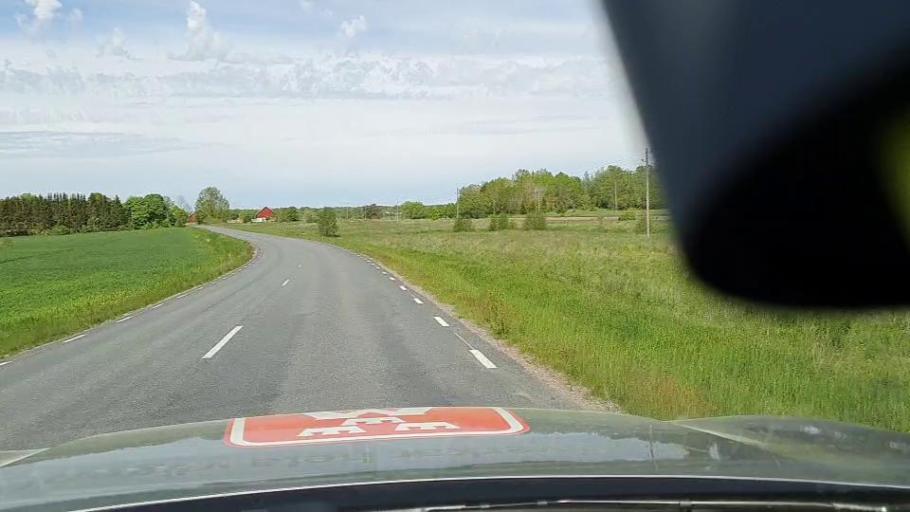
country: SE
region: Soedermanland
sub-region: Eskilstuna Kommun
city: Skogstorp
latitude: 59.3041
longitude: 16.4619
